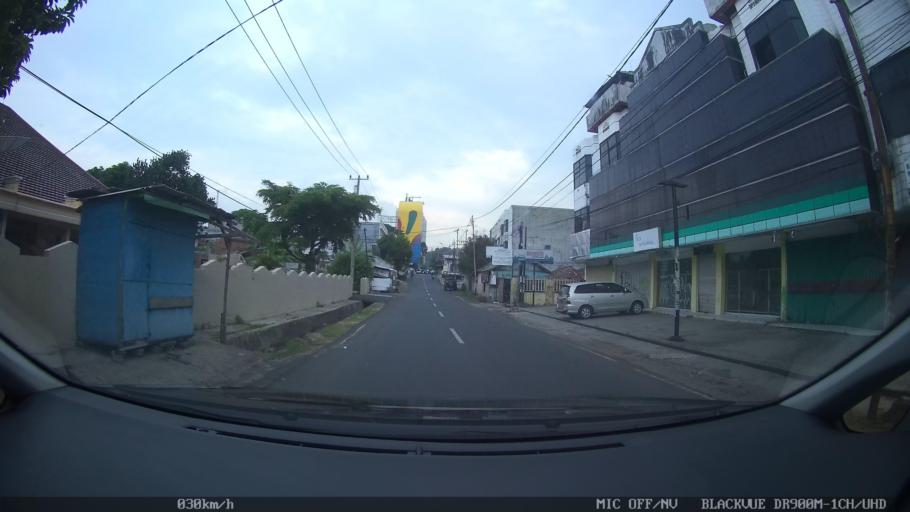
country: ID
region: Lampung
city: Bandarlampung
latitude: -5.4241
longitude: 105.2542
